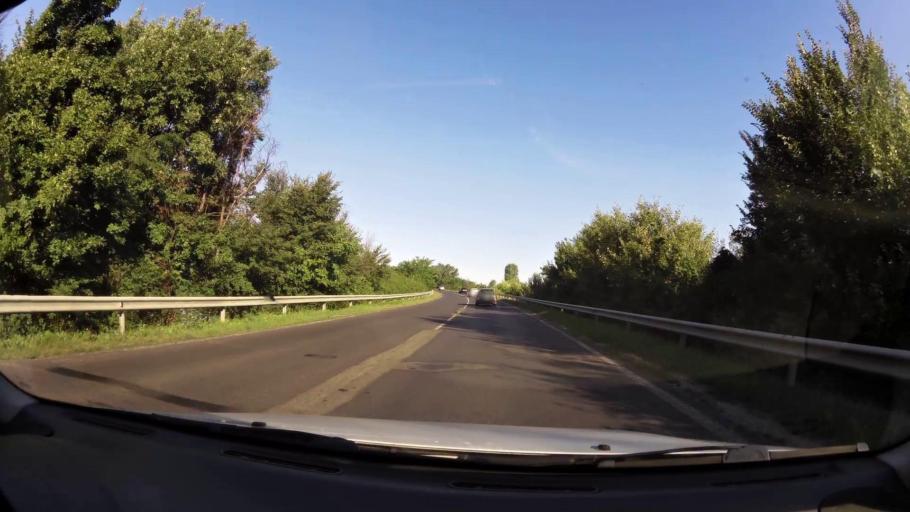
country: HU
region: Pest
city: Nyaregyhaza
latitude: 47.3154
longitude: 19.4914
